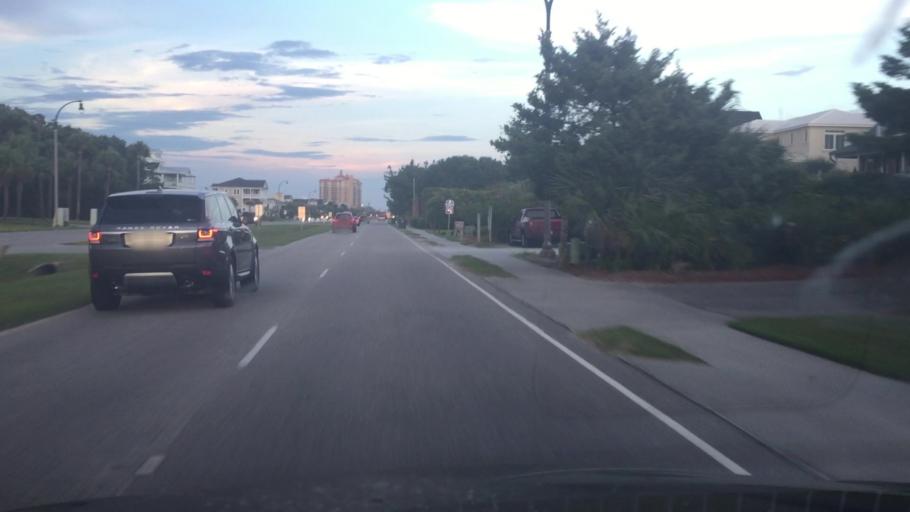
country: US
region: South Carolina
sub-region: Horry County
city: North Myrtle Beach
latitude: 33.8228
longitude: -78.6610
